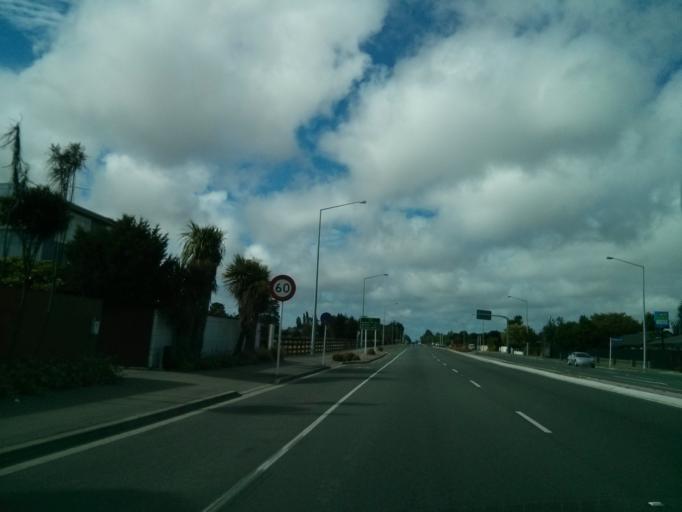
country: NZ
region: Canterbury
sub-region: Selwyn District
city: Prebbleton
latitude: -43.5197
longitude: 172.5344
